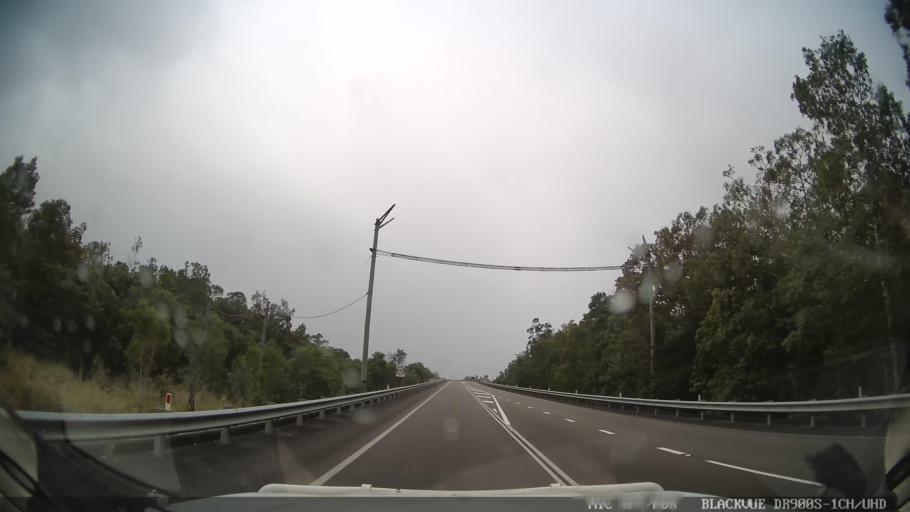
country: AU
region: Queensland
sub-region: Hinchinbrook
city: Ingham
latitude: -18.5128
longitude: 146.1879
